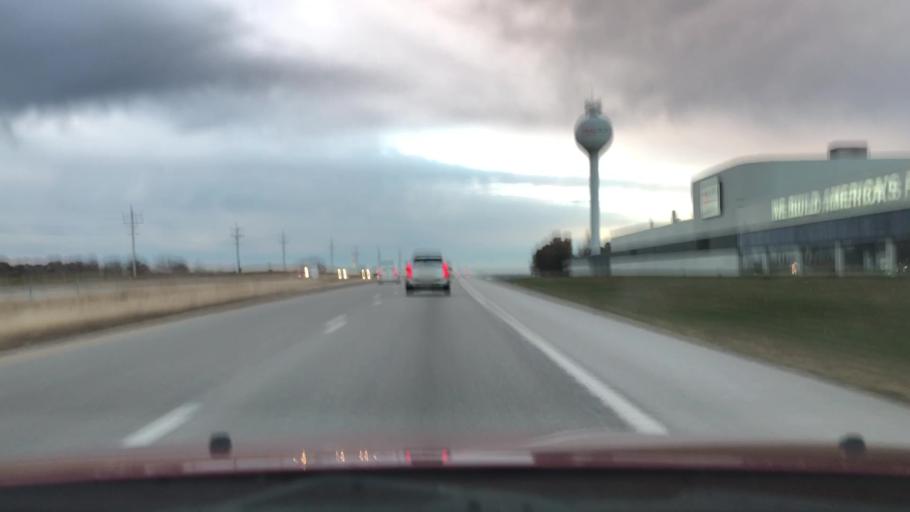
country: US
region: Missouri
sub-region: Christian County
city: Ozark
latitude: 37.0526
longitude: -93.2268
